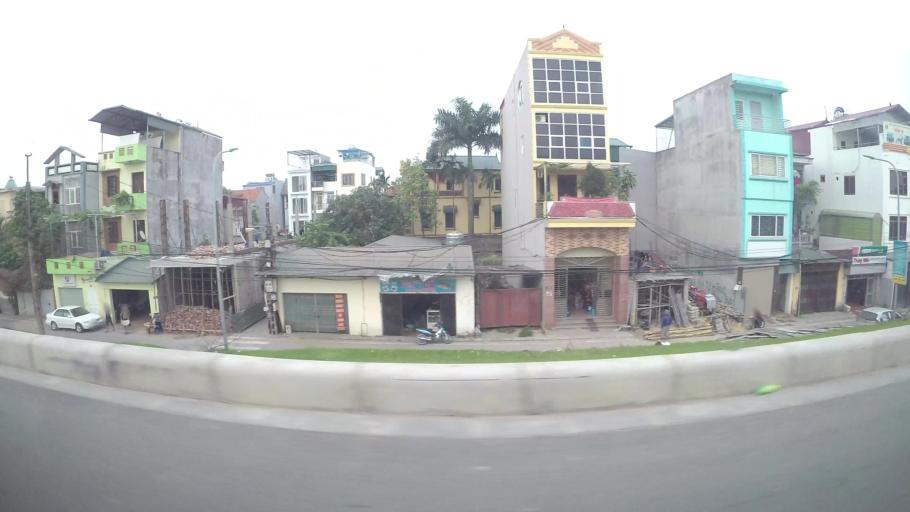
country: VN
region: Ha Noi
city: Hoan Kiem
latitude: 21.0275
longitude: 105.8825
